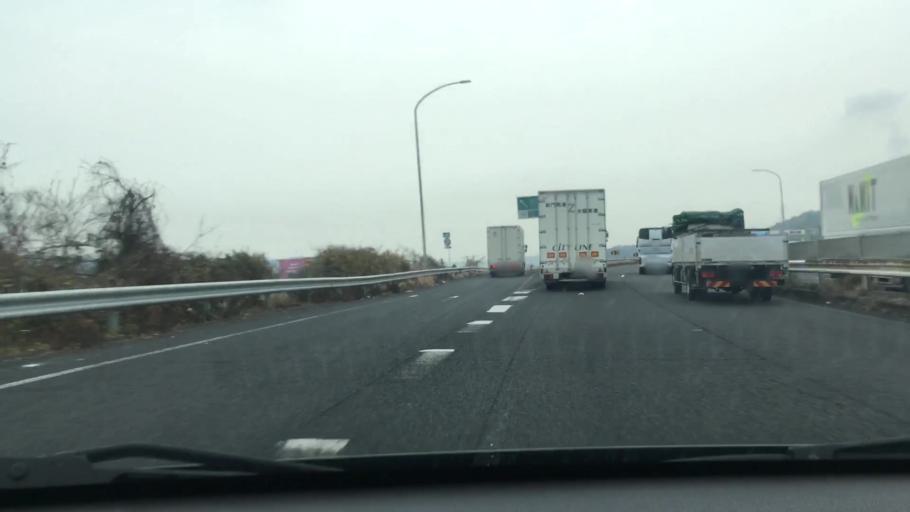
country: JP
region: Mie
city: Ueno-ebisumachi
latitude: 34.7906
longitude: 136.1618
